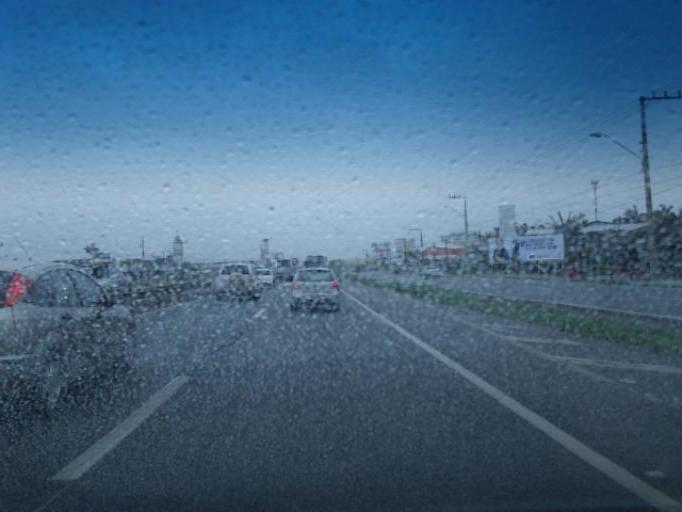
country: BR
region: Santa Catarina
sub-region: Itajai
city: Itajai
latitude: -26.8721
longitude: -48.7288
